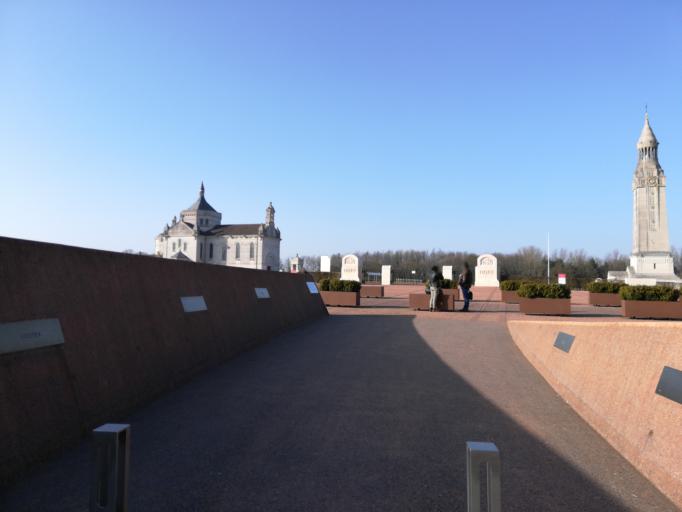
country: FR
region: Nord-Pas-de-Calais
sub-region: Departement du Pas-de-Calais
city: Ablain-Saint-Nazaire
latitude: 50.3998
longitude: 2.7197
